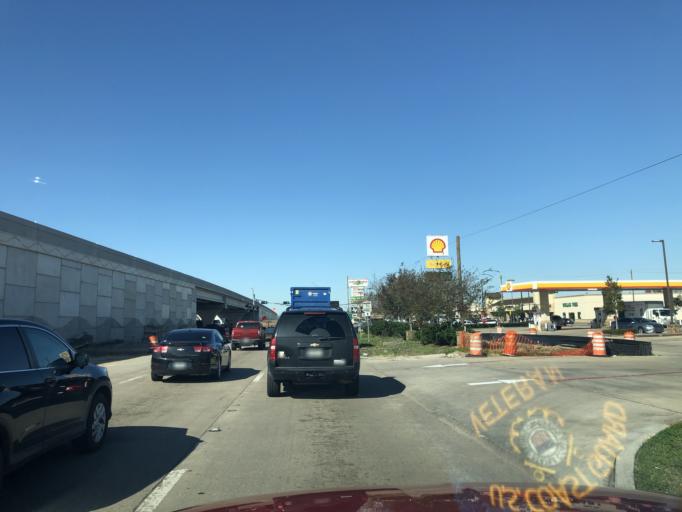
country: US
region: Texas
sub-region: Galveston County
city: League City
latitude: 29.5021
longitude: -95.1131
